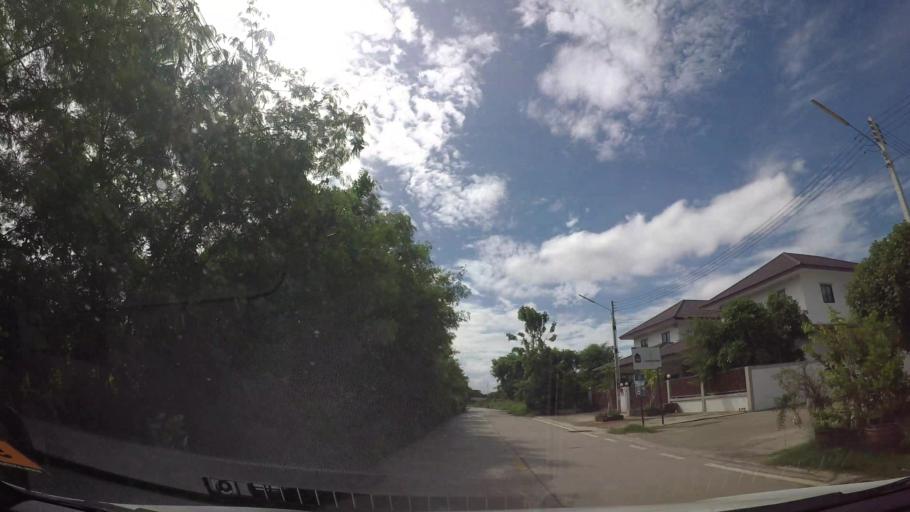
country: TH
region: Rayong
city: Rayong
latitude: 12.6668
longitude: 101.2915
